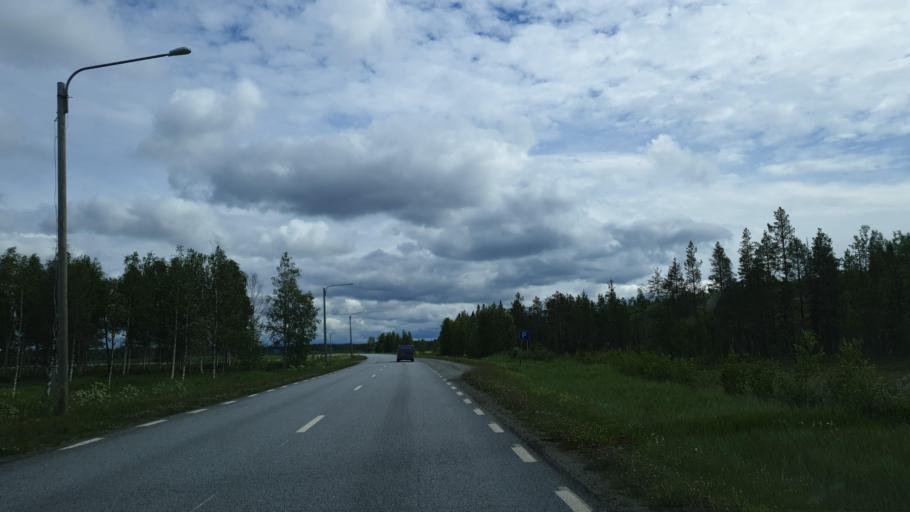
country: SE
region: Vaesterbotten
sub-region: Vilhelmina Kommun
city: Sjoberg
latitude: 64.6332
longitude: 16.3781
